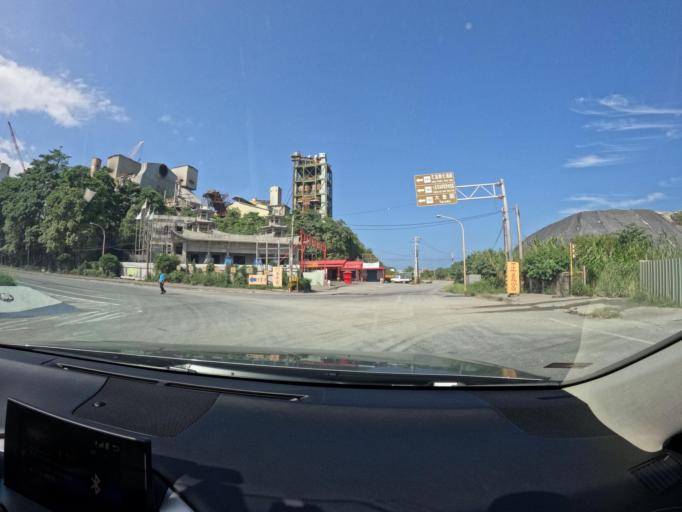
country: TW
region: Taiwan
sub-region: Hualien
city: Hualian
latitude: 24.0079
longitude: 121.6371
